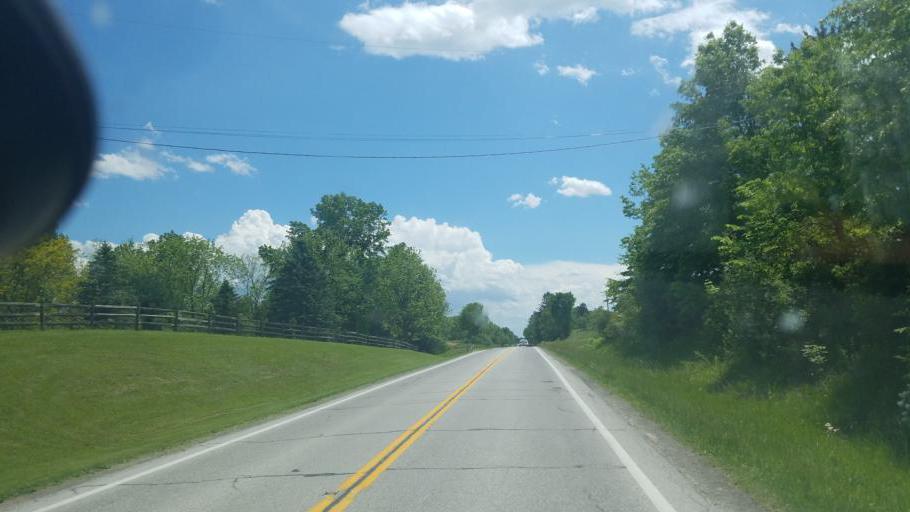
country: US
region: Ohio
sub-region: Geauga County
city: Middlefield
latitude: 41.4532
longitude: -80.9549
